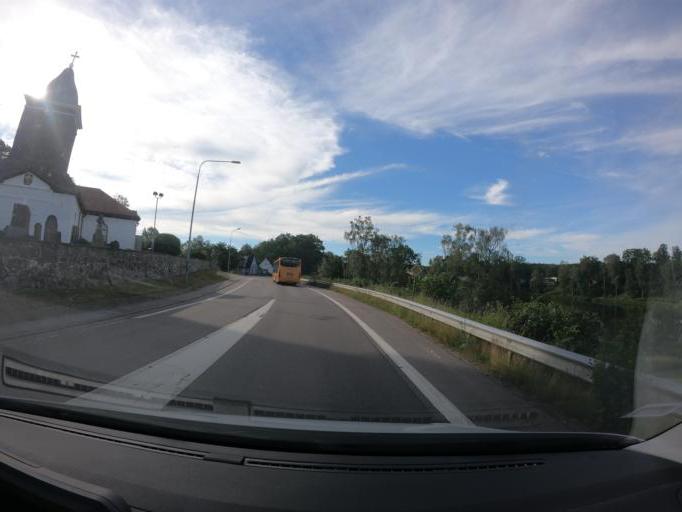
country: SE
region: Skane
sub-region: Orkelljunga Kommun
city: OErkelljunga
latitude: 56.2795
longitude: 13.2788
